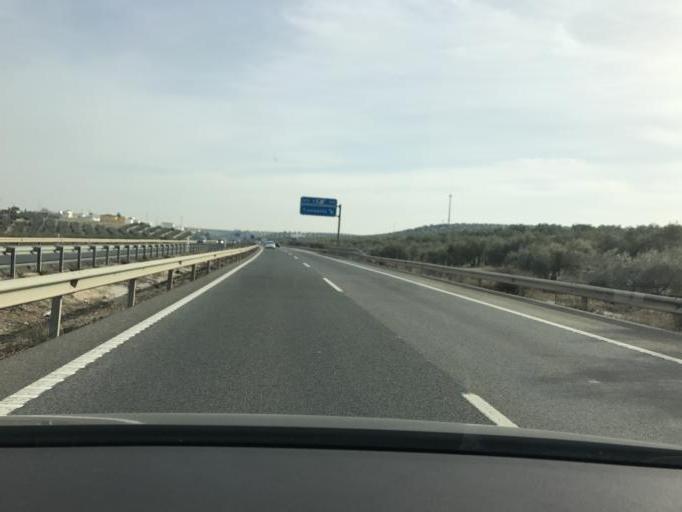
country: ES
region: Andalusia
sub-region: Provincia de Granada
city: Moraleda de Zafayona
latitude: 37.1790
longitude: -3.9118
